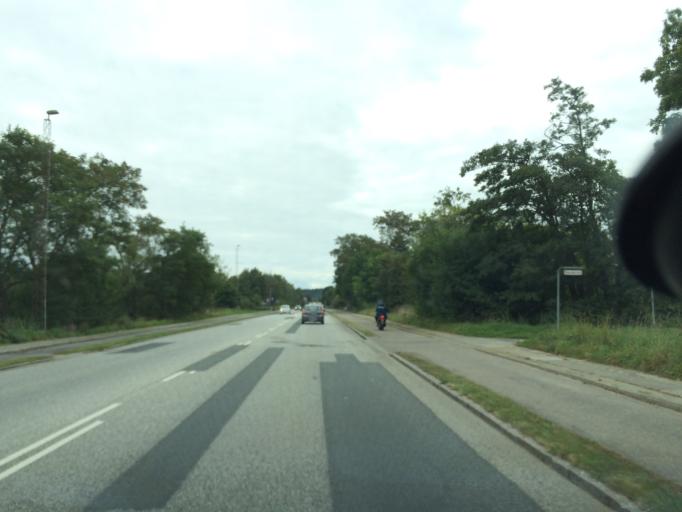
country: DK
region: South Denmark
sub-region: Aabenraa Kommune
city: Aabenraa
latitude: 55.0406
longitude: 9.4058
